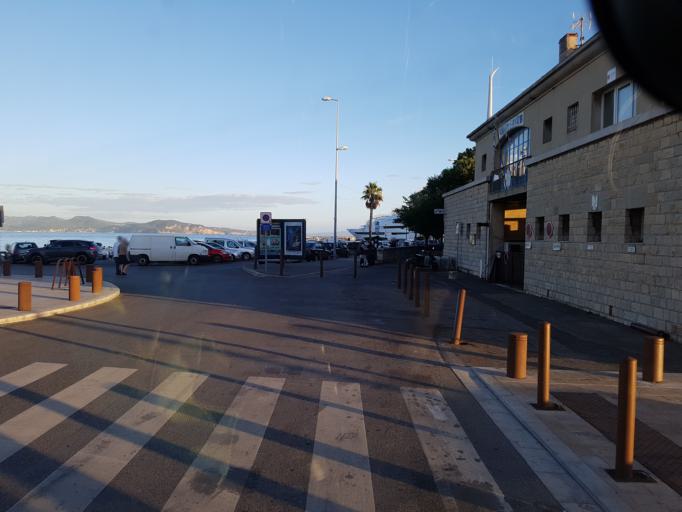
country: FR
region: Provence-Alpes-Cote d'Azur
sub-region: Departement des Bouches-du-Rhone
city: La Ciotat
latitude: 43.1736
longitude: 5.6106
